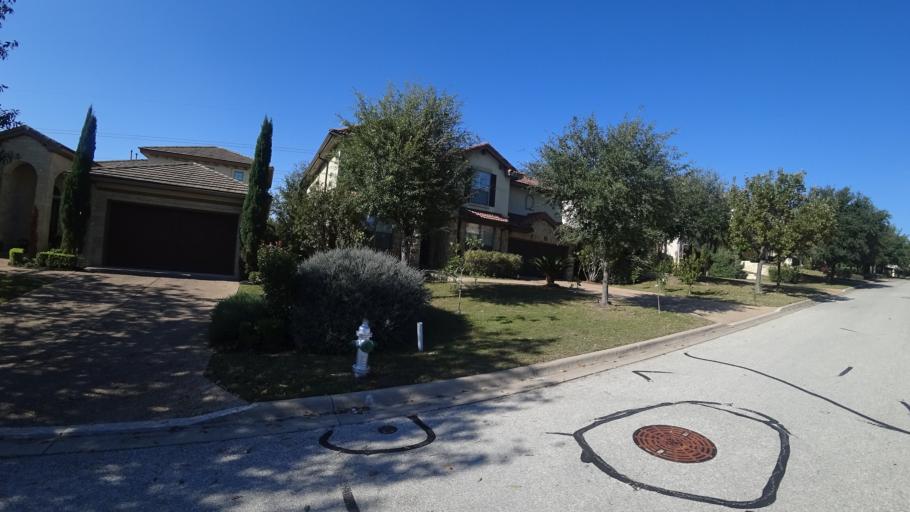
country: US
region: Texas
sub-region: Travis County
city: Hudson Bend
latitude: 30.3588
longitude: -97.8865
